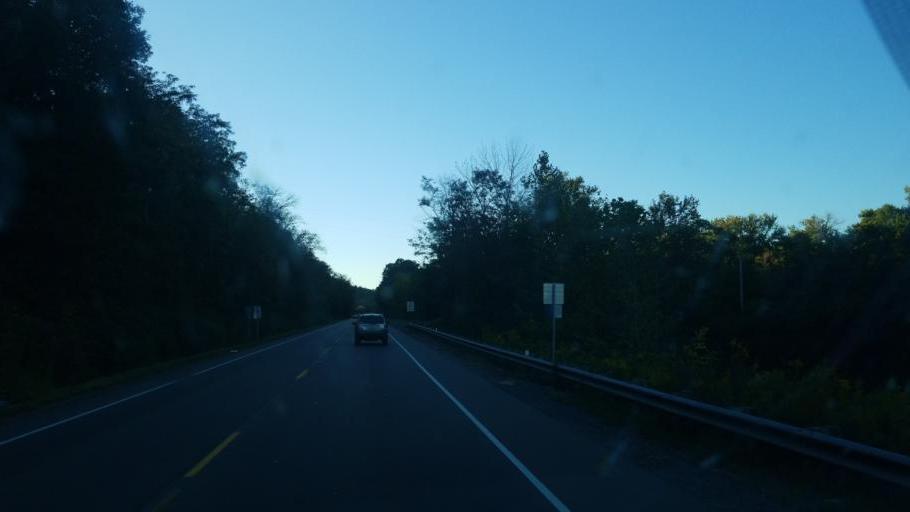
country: US
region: Ohio
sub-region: Coshocton County
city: Coshocton
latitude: 40.2848
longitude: -81.8775
